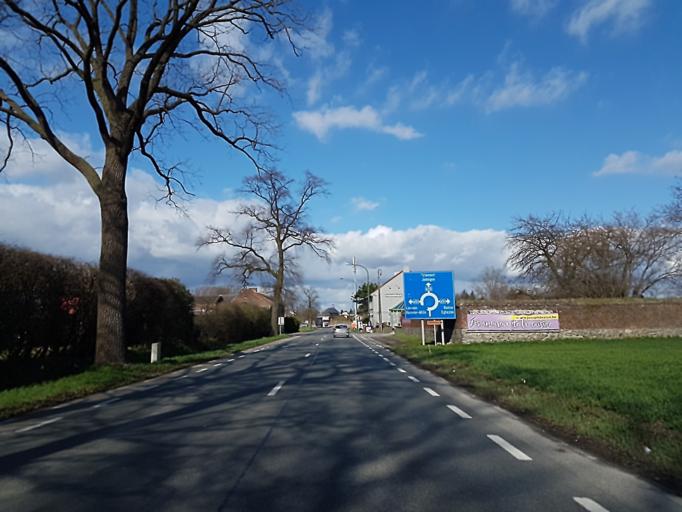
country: BE
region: Wallonia
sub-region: Province du Brabant Wallon
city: Incourt
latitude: 50.6700
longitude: 4.8232
